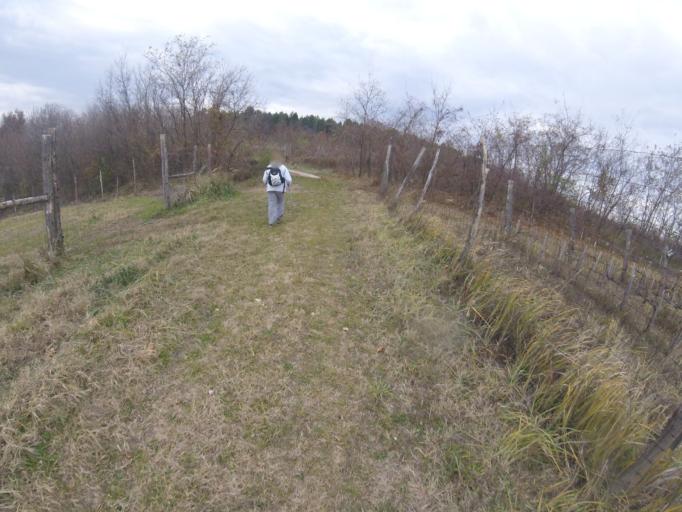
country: HU
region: Tolna
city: Szekszard
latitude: 46.3244
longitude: 18.6772
